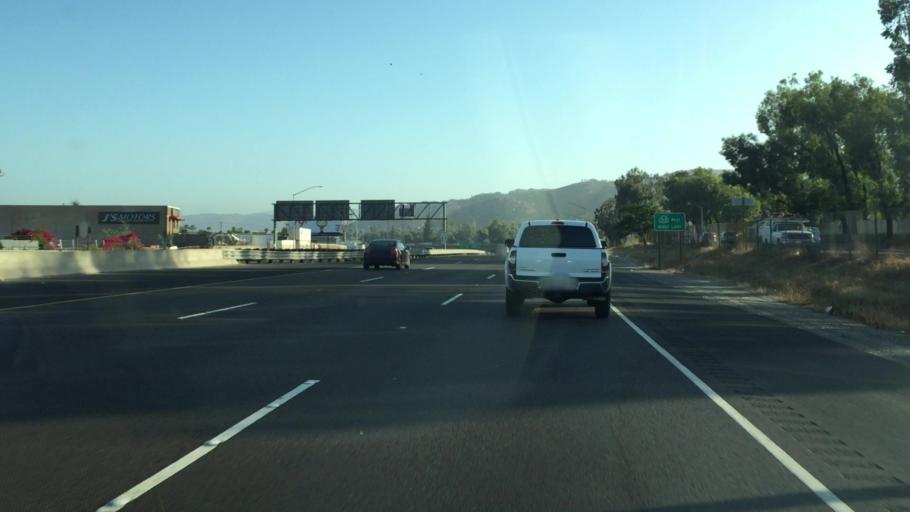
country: US
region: California
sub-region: San Diego County
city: El Cajon
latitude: 32.8145
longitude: -116.9614
